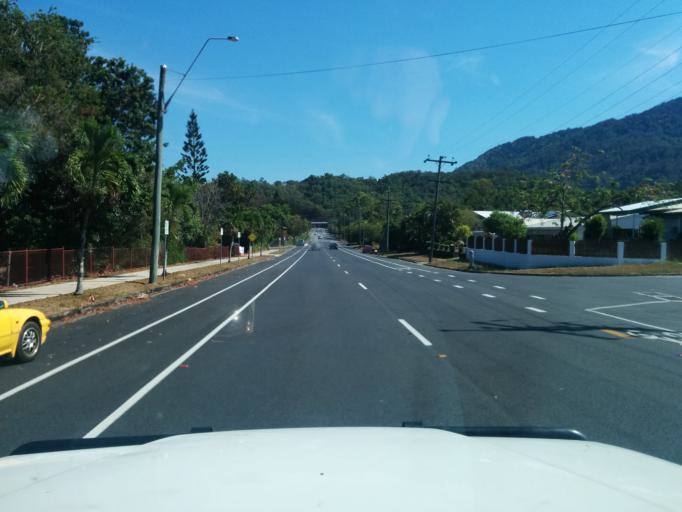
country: AU
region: Queensland
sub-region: Cairns
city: Redlynch
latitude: -16.9085
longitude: 145.7284
